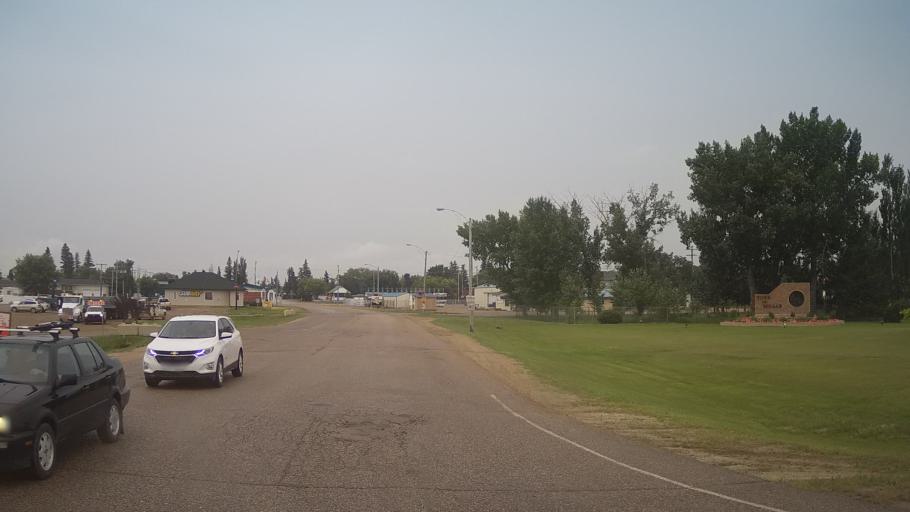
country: CA
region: Saskatchewan
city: Biggar
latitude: 52.0623
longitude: -107.9805
